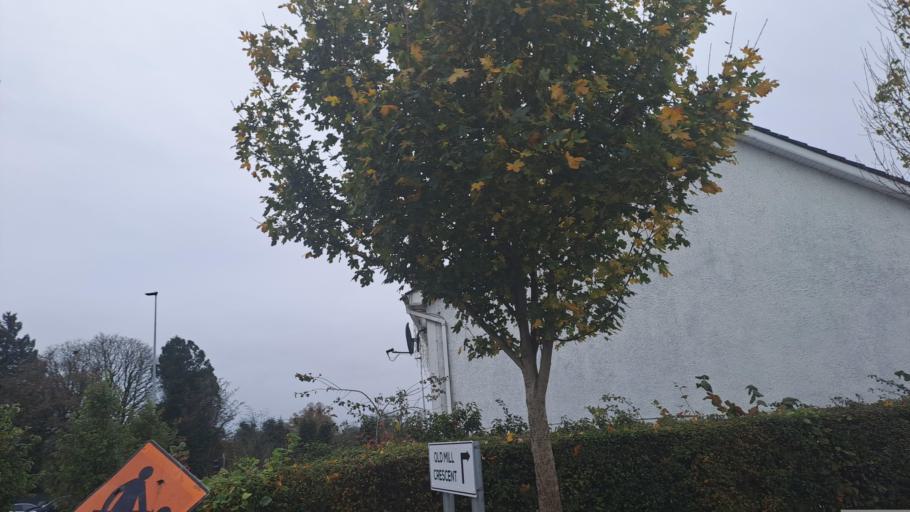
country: IE
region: Ulster
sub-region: An Cabhan
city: Virginia
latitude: 53.8347
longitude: -7.0770
